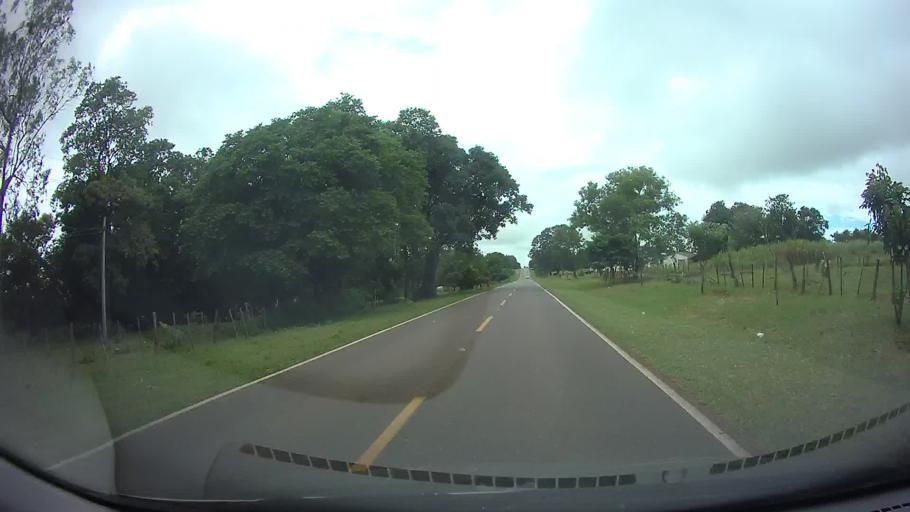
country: PY
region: Paraguari
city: Acahay
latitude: -25.9464
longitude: -57.0955
